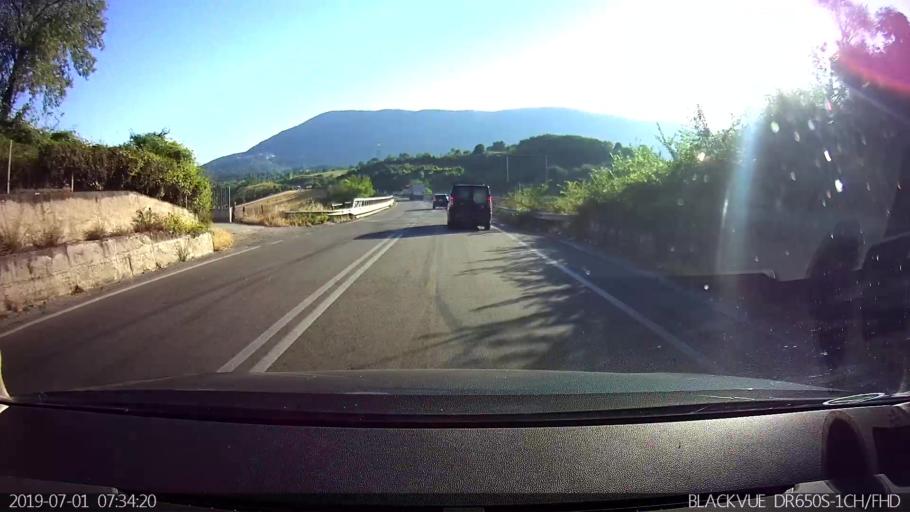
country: IT
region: Latium
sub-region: Provincia di Latina
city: Prossedi
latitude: 41.5151
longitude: 13.2709
